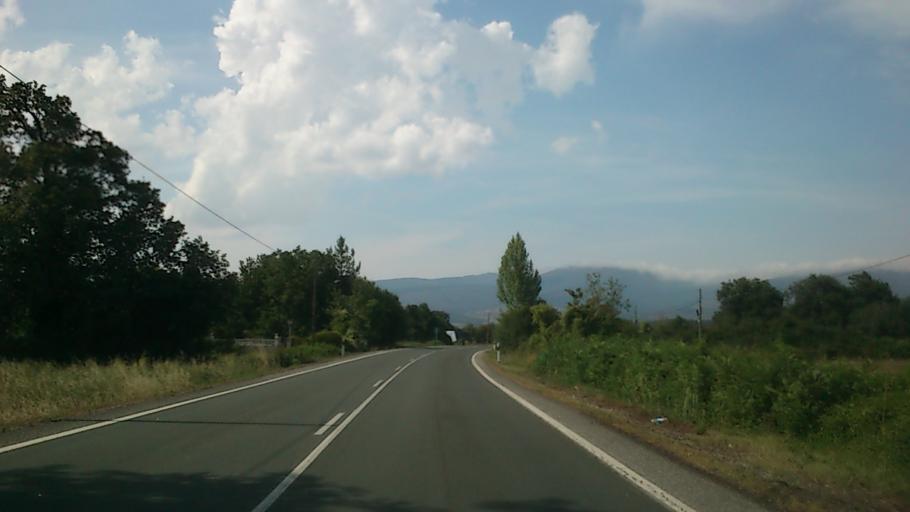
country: ES
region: Castille and Leon
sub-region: Provincia de Burgos
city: Espinosa de los Monteros
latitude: 43.0540
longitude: -3.4907
